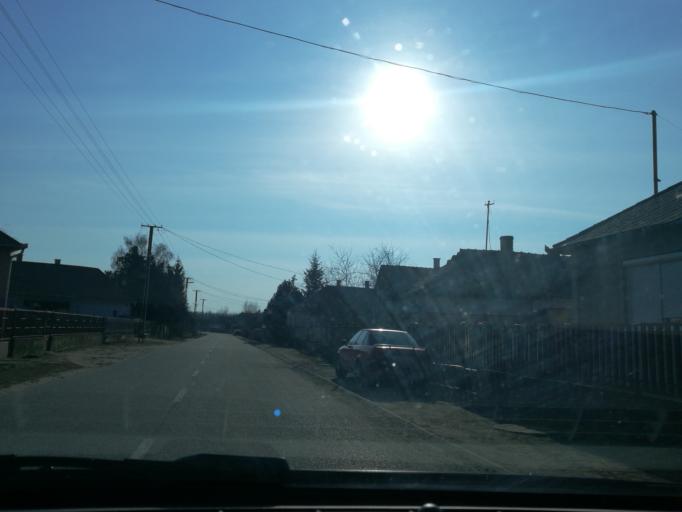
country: HU
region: Szabolcs-Szatmar-Bereg
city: Nyirbogdany
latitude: 48.0575
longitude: 21.9399
